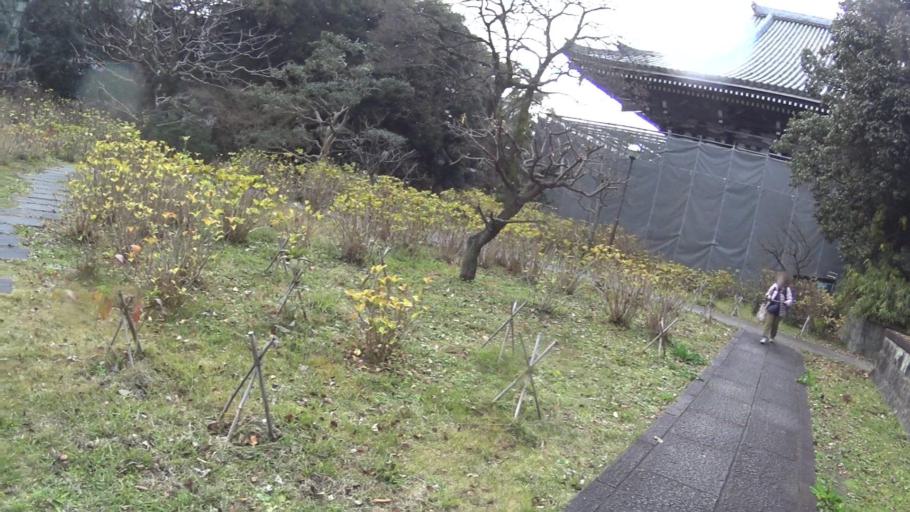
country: JP
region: Kyoto
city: Kyoto
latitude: 34.9880
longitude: 135.7769
